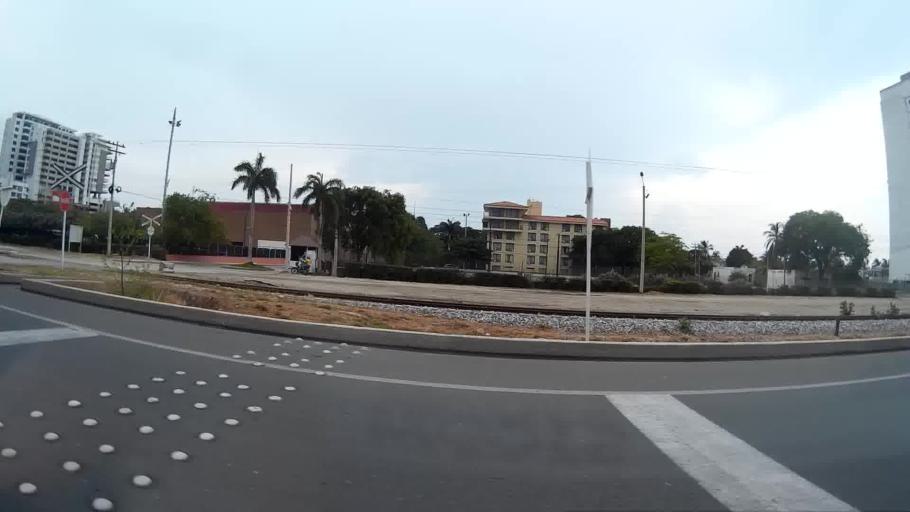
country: CO
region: Magdalena
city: Santa Marta
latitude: 11.1684
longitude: -74.2292
